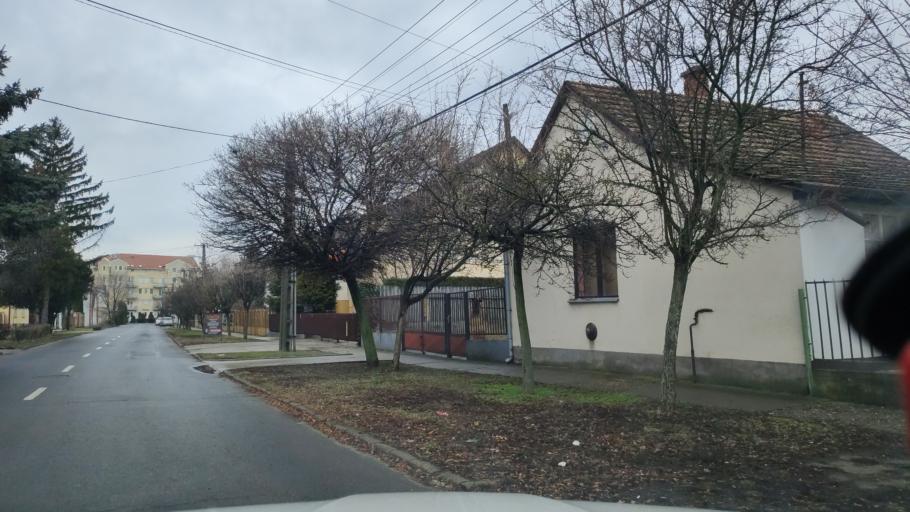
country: HU
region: Hajdu-Bihar
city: Hajduszoboszlo
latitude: 47.4465
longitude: 21.4011
